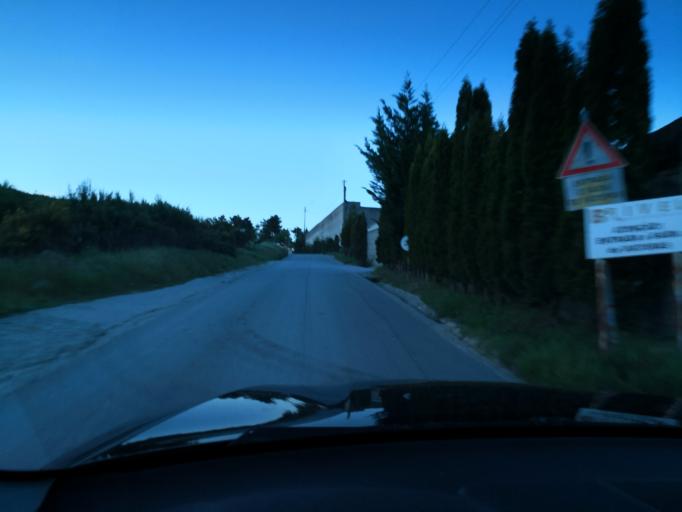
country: PT
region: Vila Real
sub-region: Vila Real
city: Vila Real
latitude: 41.3430
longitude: -7.6954
